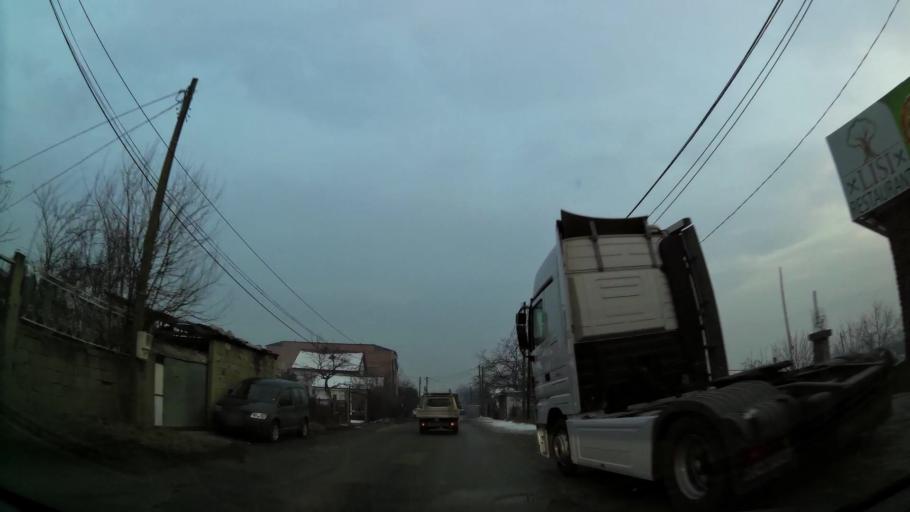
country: MK
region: Suto Orizari
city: Suto Orizare
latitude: 42.0264
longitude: 21.4109
